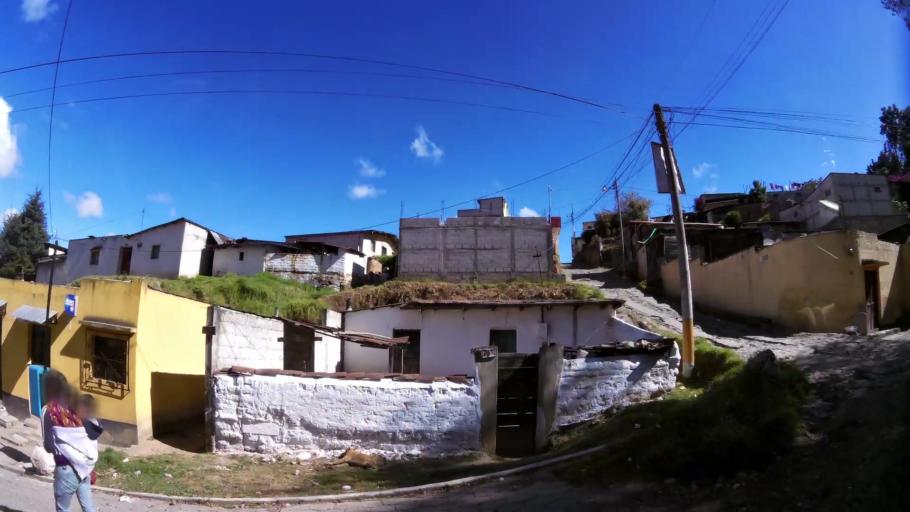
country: GT
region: Quetzaltenango
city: Quetzaltenango
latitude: 14.8363
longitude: -91.5009
